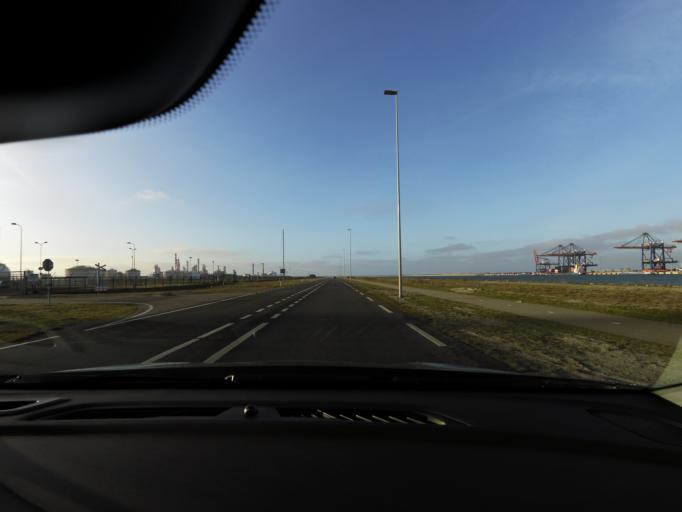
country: NL
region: South Holland
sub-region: Gemeente Rotterdam
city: Hoek van Holland
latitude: 51.9684
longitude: 4.0356
